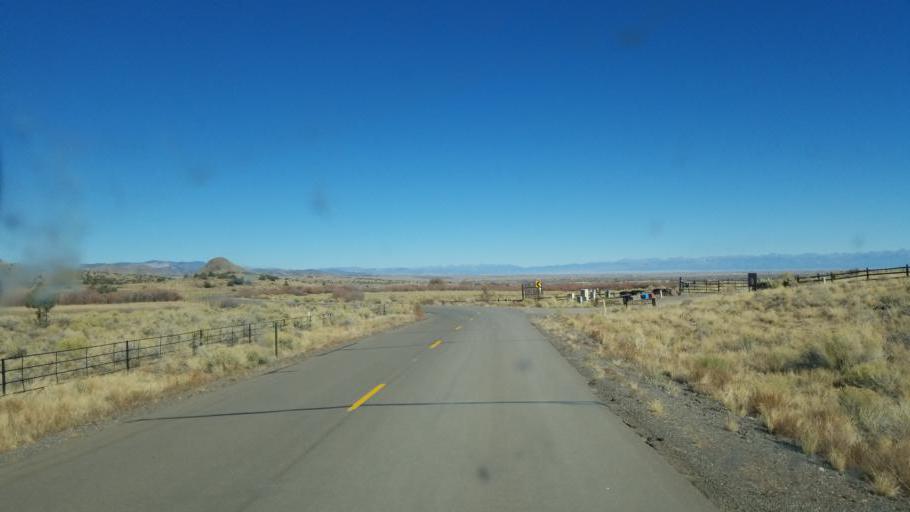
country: US
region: Colorado
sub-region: Rio Grande County
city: Del Norte
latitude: 37.6396
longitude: -106.3652
